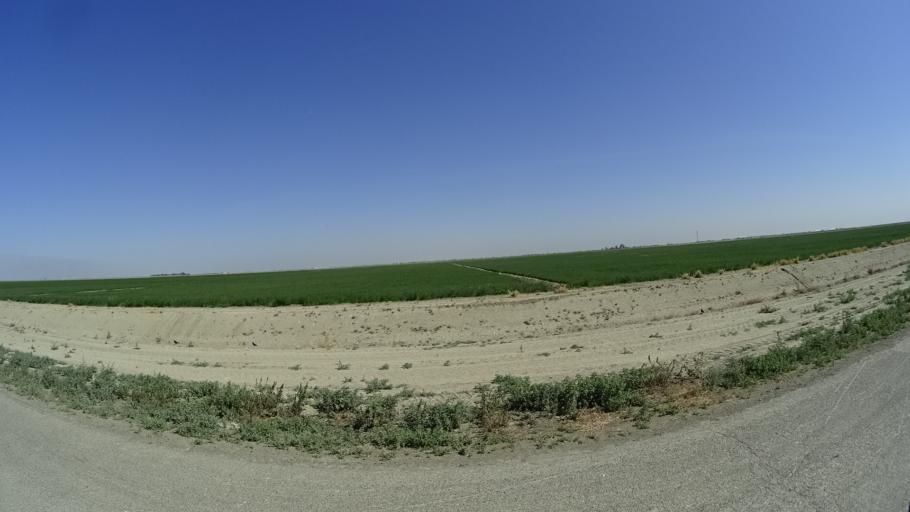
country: US
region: California
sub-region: Kings County
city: Corcoran
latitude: 36.0072
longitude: -119.5508
